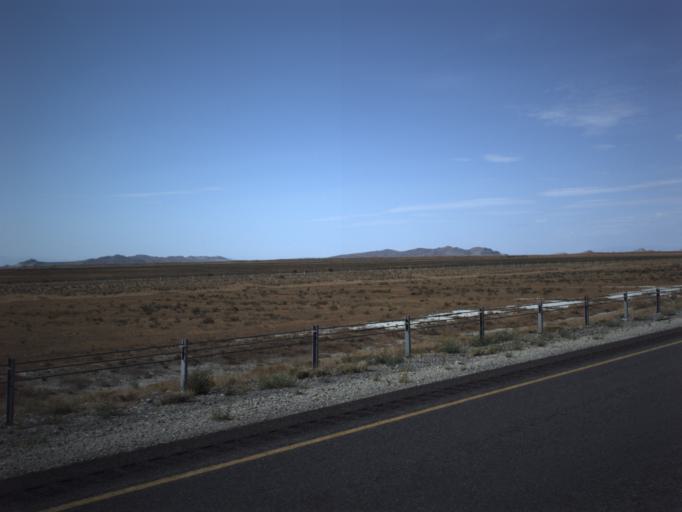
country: US
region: Utah
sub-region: Tooele County
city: Grantsville
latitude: 40.7264
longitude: -113.1745
